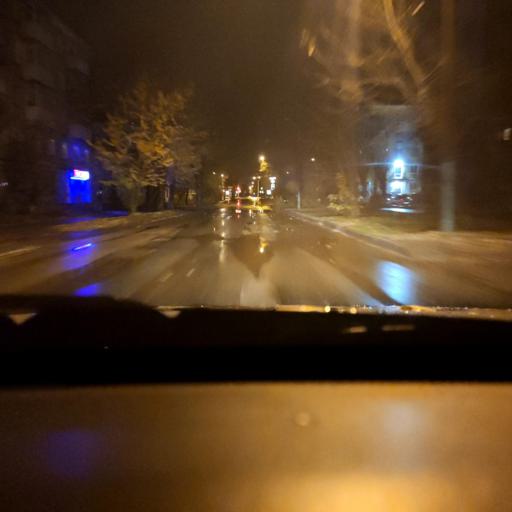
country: RU
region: Perm
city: Kultayevo
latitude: 58.0023
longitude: 55.9524
